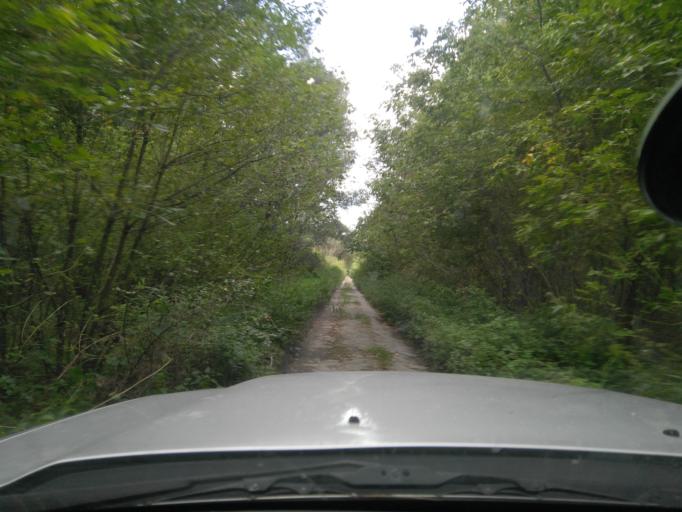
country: HU
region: Bacs-Kiskun
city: Apostag
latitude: 46.8948
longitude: 18.9450
